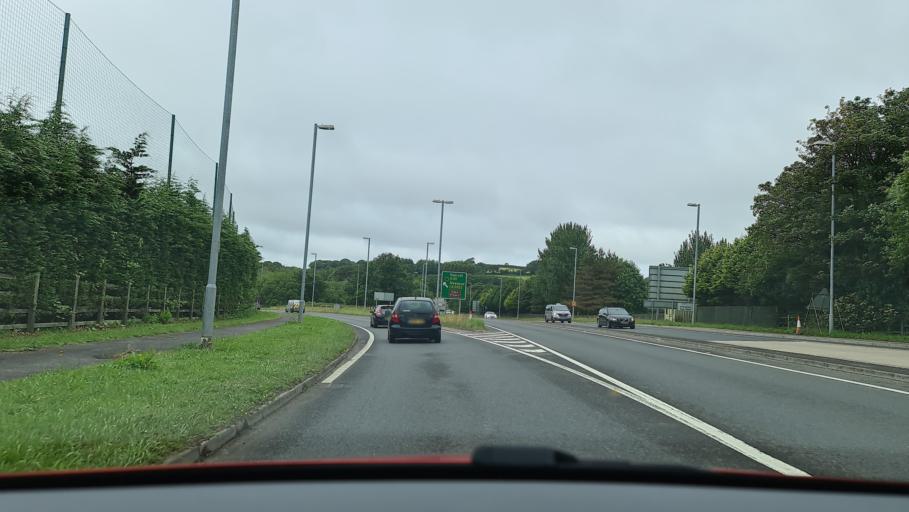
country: GB
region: England
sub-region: Cornwall
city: Bodmin
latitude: 50.4585
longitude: -4.6889
